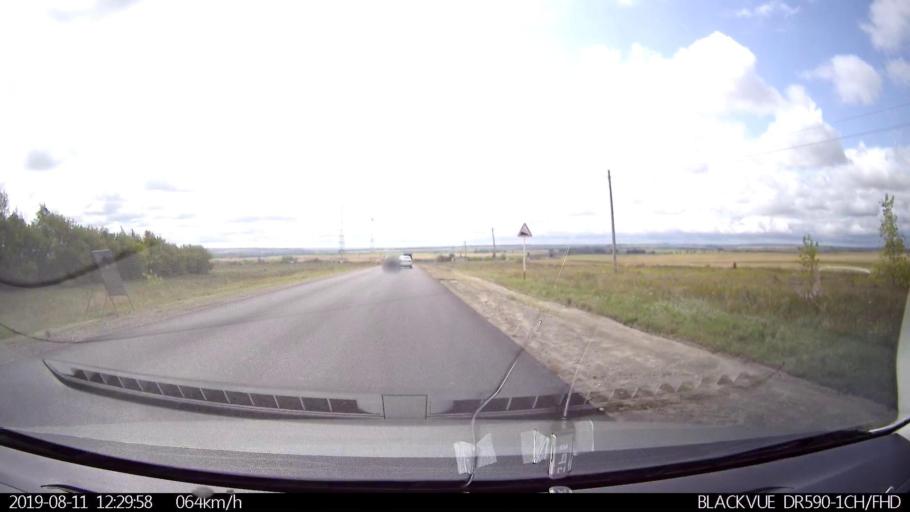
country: RU
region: Ulyanovsk
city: Ignatovka
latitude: 53.8298
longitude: 47.8979
